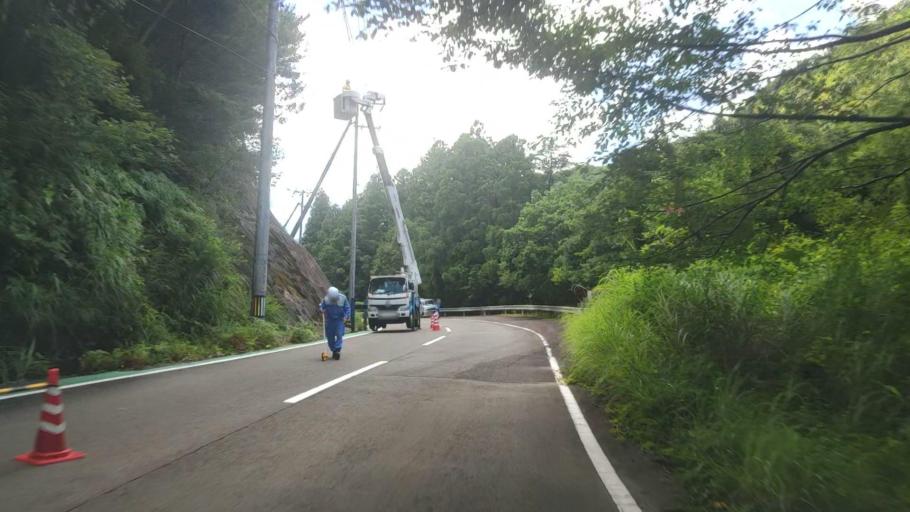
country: JP
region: Wakayama
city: Shingu
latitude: 33.9594
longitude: 135.9956
